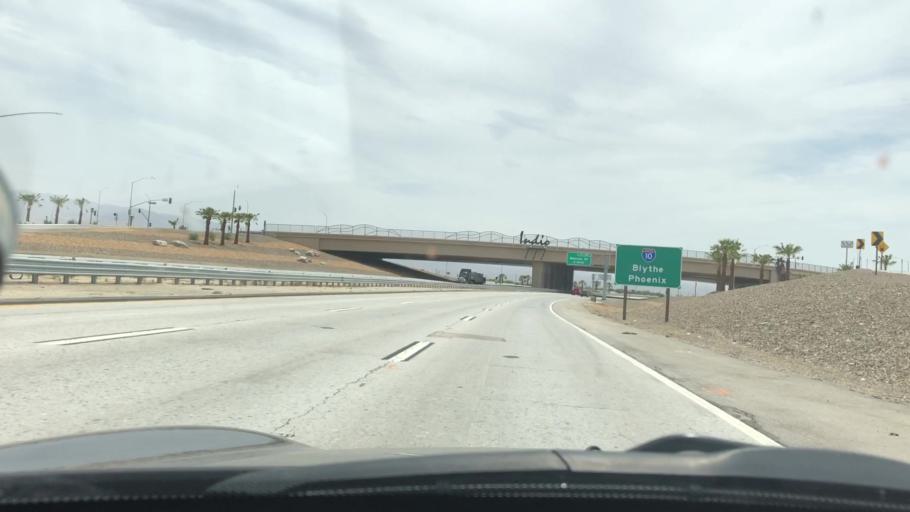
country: US
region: California
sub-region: Riverside County
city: Bermuda Dunes
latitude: 33.7500
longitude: -116.2716
